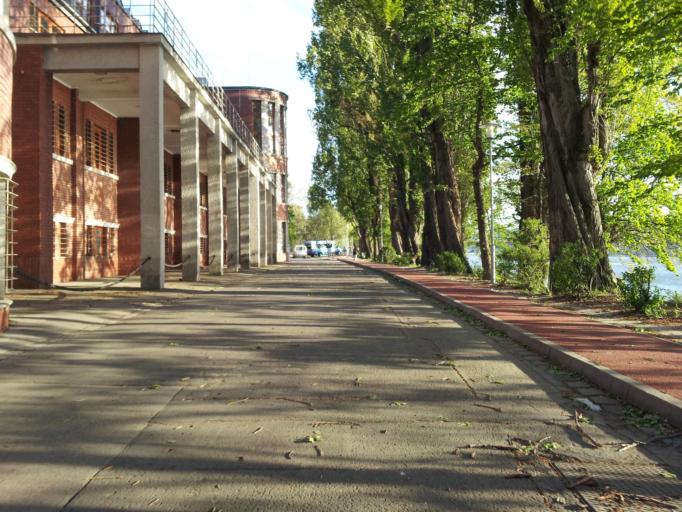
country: HU
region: Budapest
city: Budapest II. keruelet
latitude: 47.5212
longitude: 19.0421
